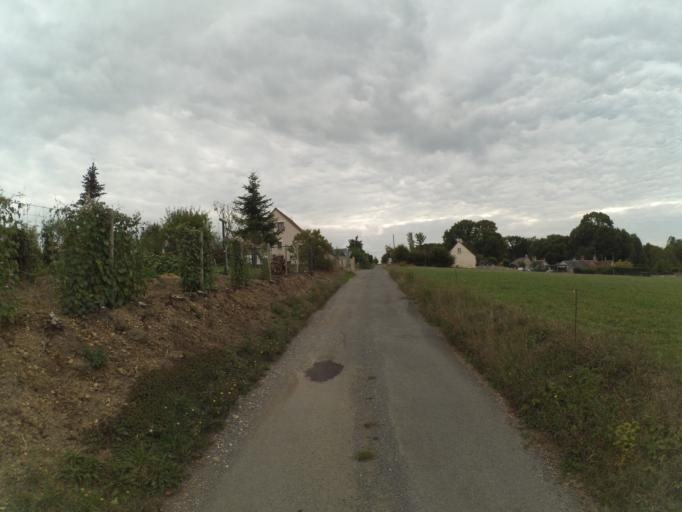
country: FR
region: Centre
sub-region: Departement d'Indre-et-Loire
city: Auzouer-en-Touraine
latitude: 47.5103
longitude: 0.9185
